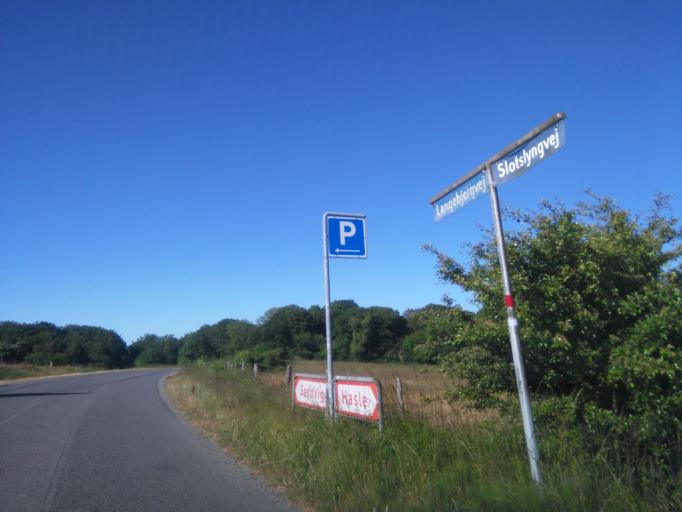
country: DK
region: Capital Region
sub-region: Bornholm Kommune
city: Ronne
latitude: 55.2748
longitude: 14.7616
